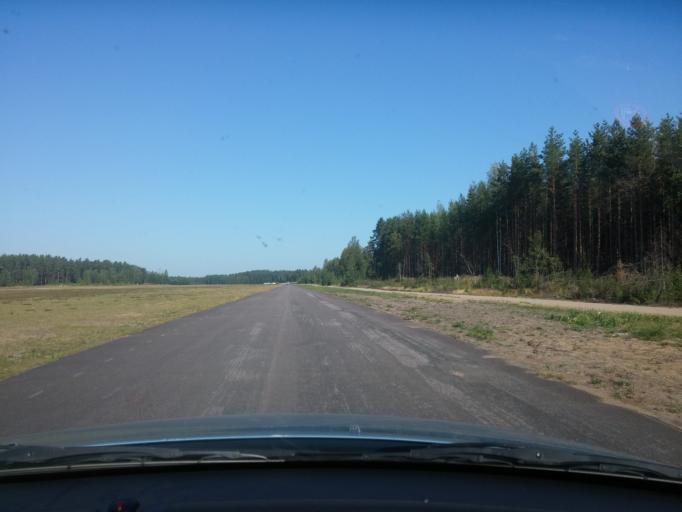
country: FI
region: Uusimaa
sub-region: Helsinki
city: Kaerkoelae
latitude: 60.7478
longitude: 24.1079
